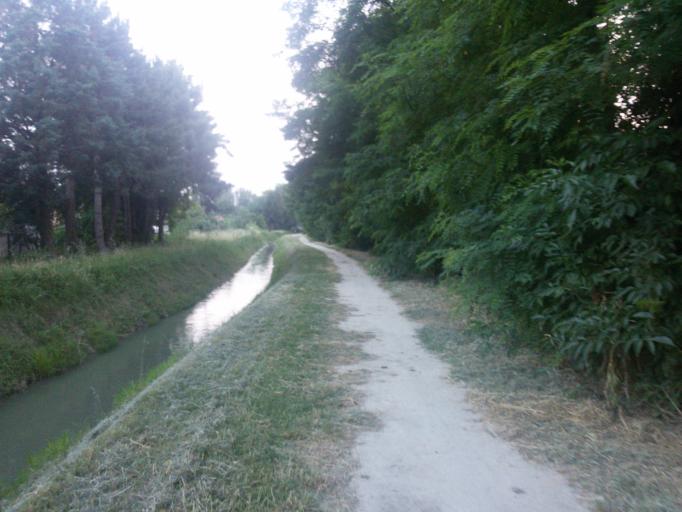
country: IT
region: Emilia-Romagna
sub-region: Provincia di Ravenna
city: Lugo
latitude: 44.4218
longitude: 11.9015
